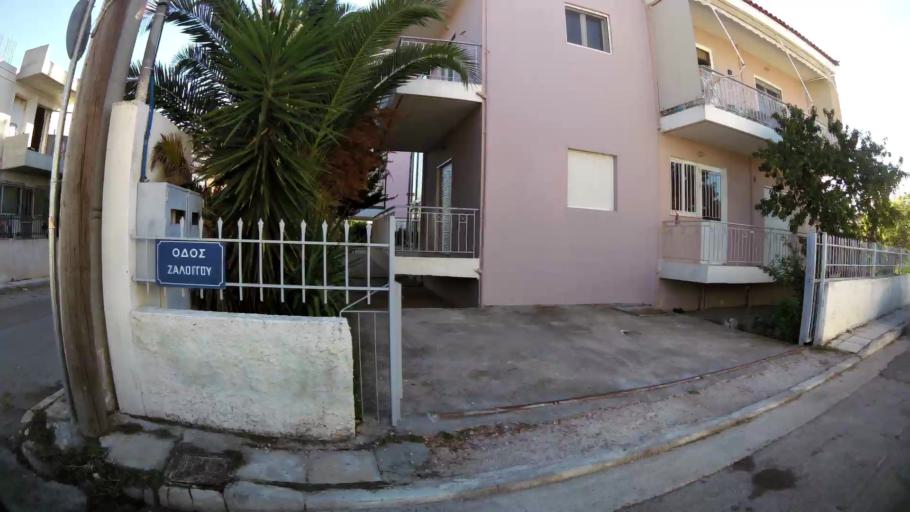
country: GR
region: Attica
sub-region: Nomarchia Anatolikis Attikis
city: Koropi
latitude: 37.9078
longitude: 23.8687
